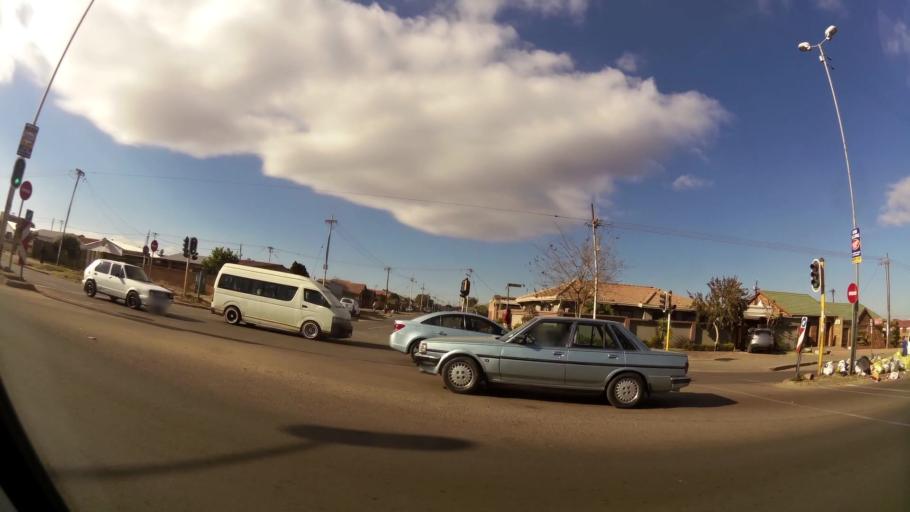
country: ZA
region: Gauteng
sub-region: City of Tshwane Metropolitan Municipality
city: Cullinan
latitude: -25.7099
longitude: 28.3820
